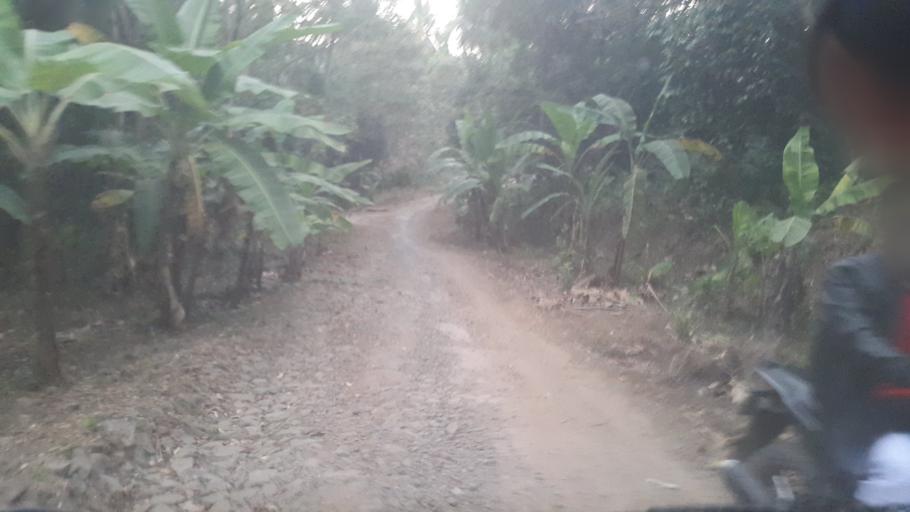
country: ID
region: West Java
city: Bojonggaling
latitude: -6.9612
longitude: 106.6038
